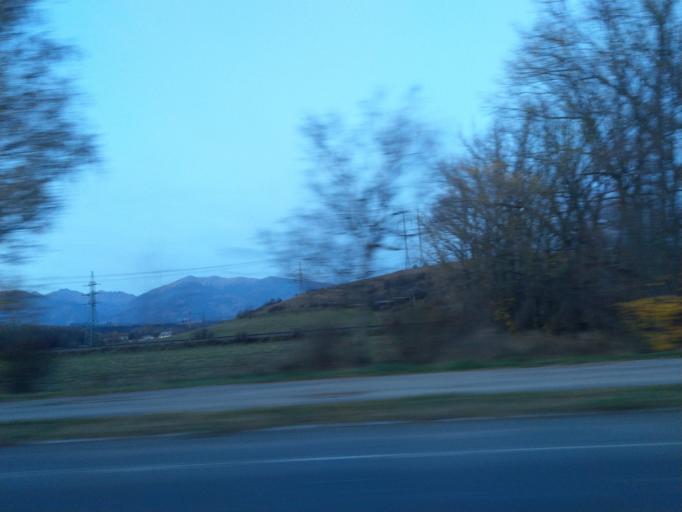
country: SK
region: Zilinsky
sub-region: Okres Zilina
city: Liptovsky Hradok
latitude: 49.0670
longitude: 19.6795
